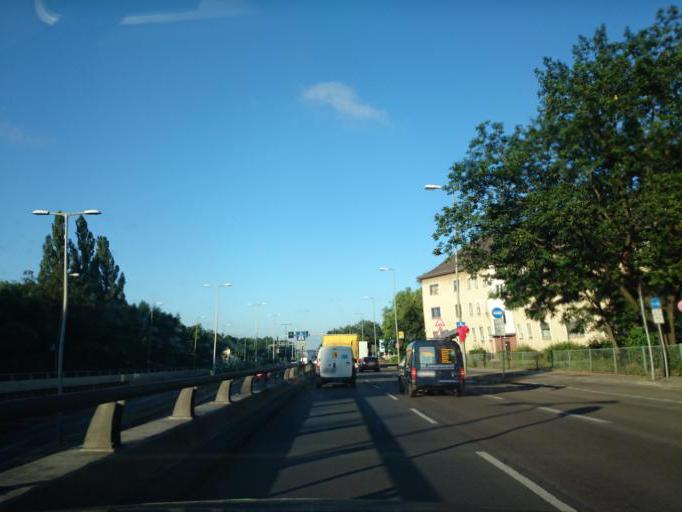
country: DE
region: Berlin
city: Tegel
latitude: 52.5548
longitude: 13.3063
